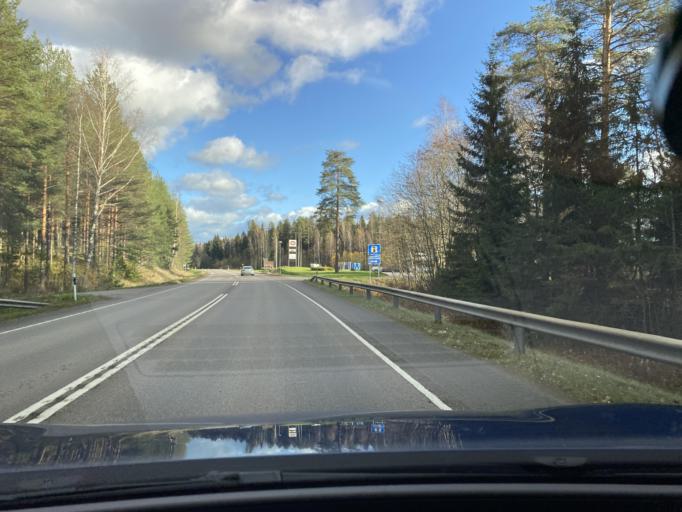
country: FI
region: Haeme
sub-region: Riihimaeki
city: Oitti
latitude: 60.7922
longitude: 24.9939
